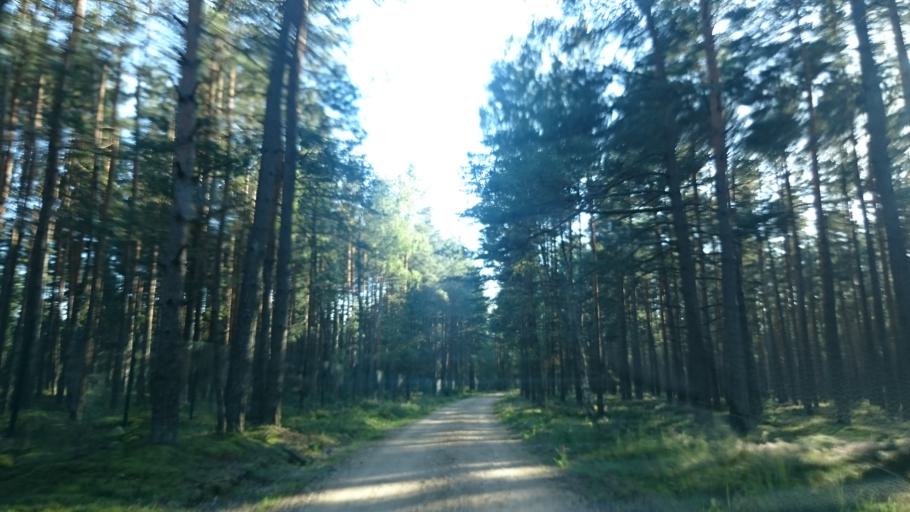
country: LV
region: Carnikava
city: Carnikava
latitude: 57.1058
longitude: 24.2344
